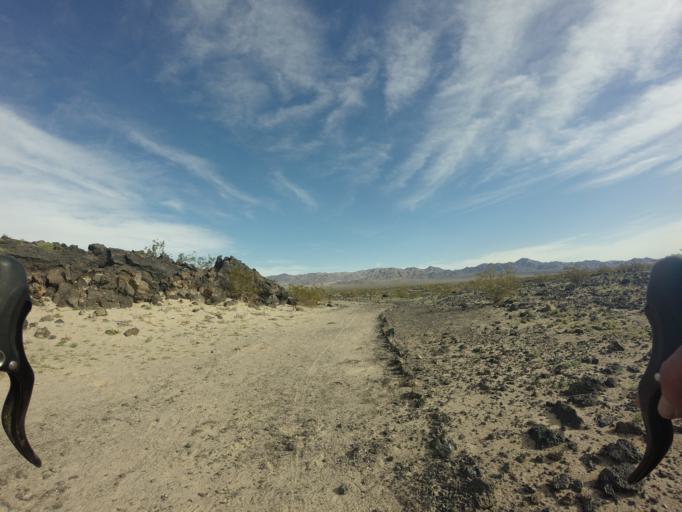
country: US
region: California
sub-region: San Bernardino County
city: Twentynine Palms
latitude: 34.5514
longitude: -115.7848
